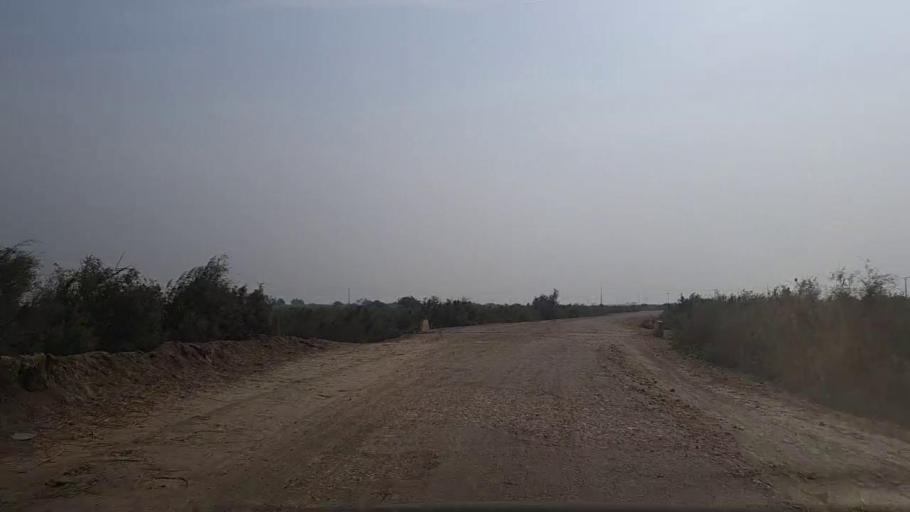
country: PK
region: Sindh
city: Mirpur Sakro
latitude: 24.3988
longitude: 67.7515
